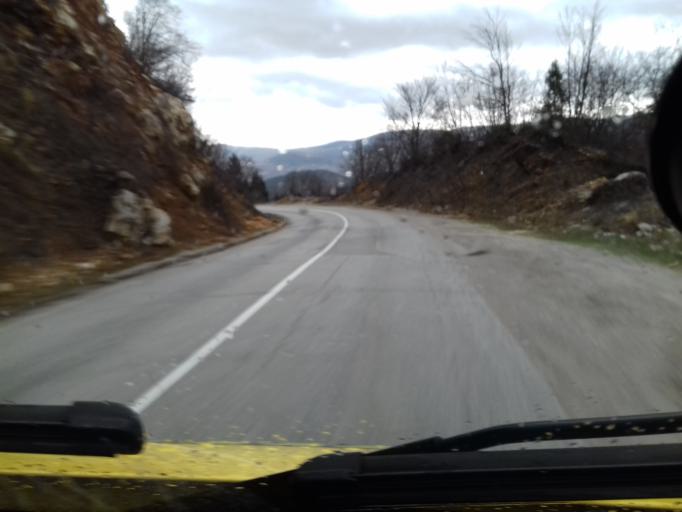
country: BA
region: Federation of Bosnia and Herzegovina
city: Turbe
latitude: 44.2731
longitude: 17.5138
